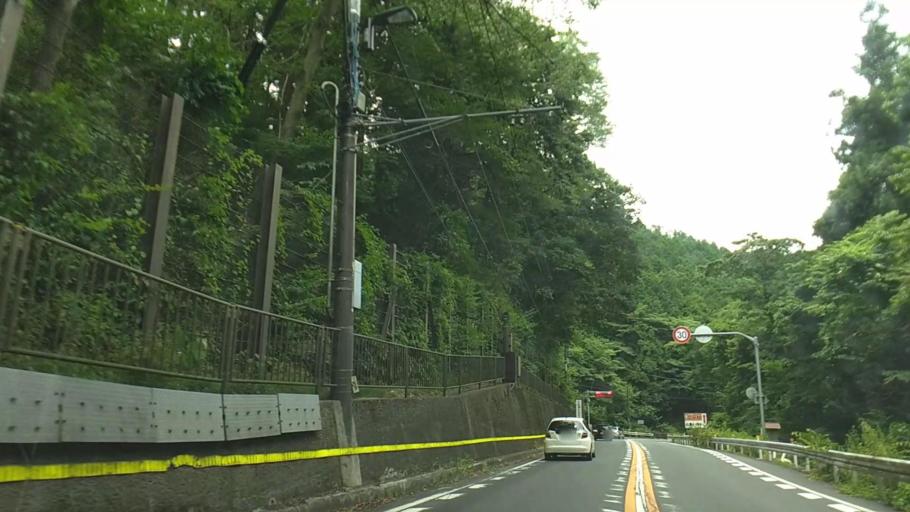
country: JP
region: Tokyo
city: Hachioji
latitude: 35.6202
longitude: 139.2349
